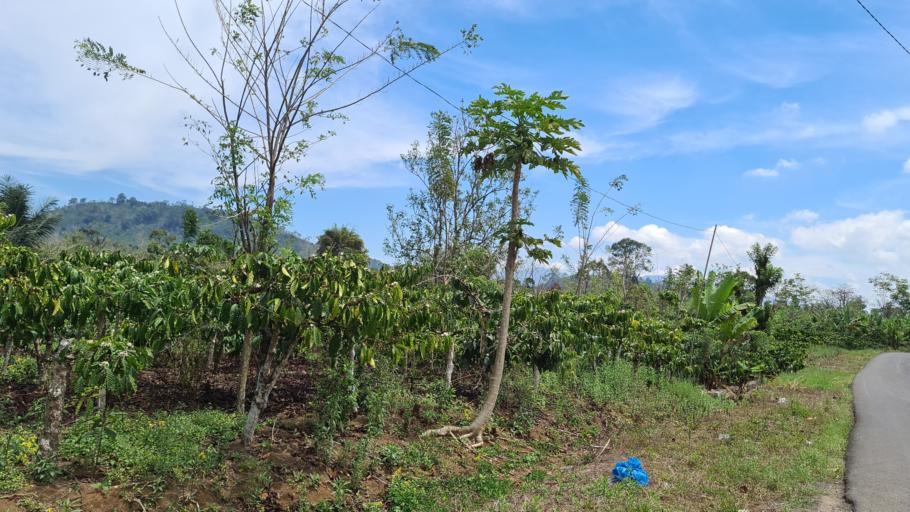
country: ID
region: Lampung
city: Kenali
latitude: -5.0966
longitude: 104.4338
